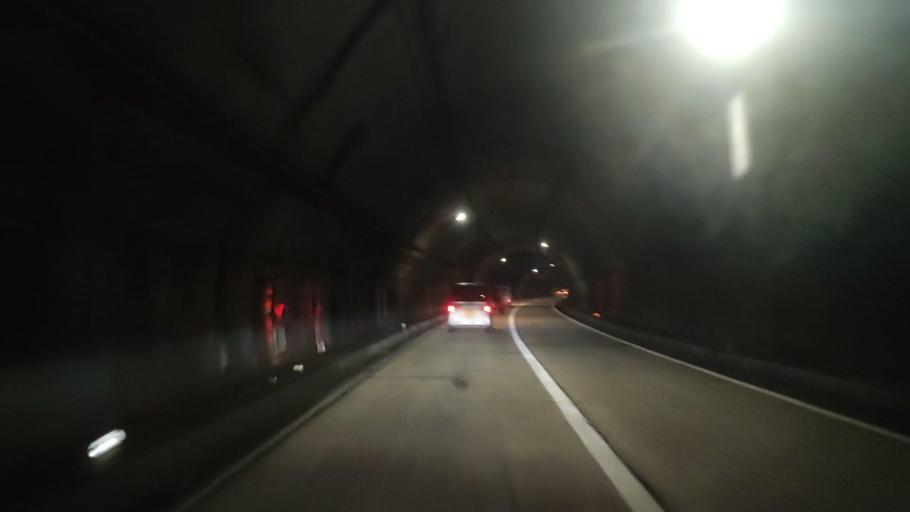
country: JP
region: Wakayama
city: Tanabe
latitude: 33.7786
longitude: 135.5030
